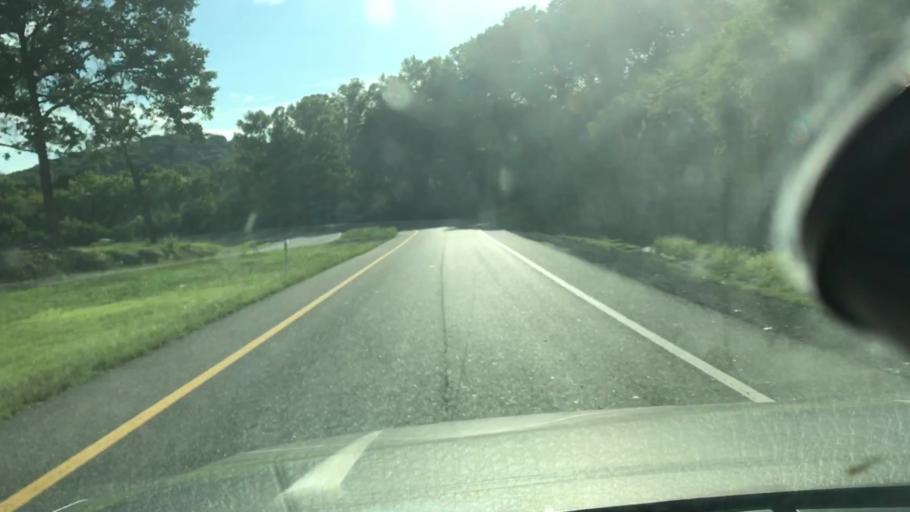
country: US
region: Tennessee
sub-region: Davidson County
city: Belle Meade
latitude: 36.1322
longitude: -86.8986
